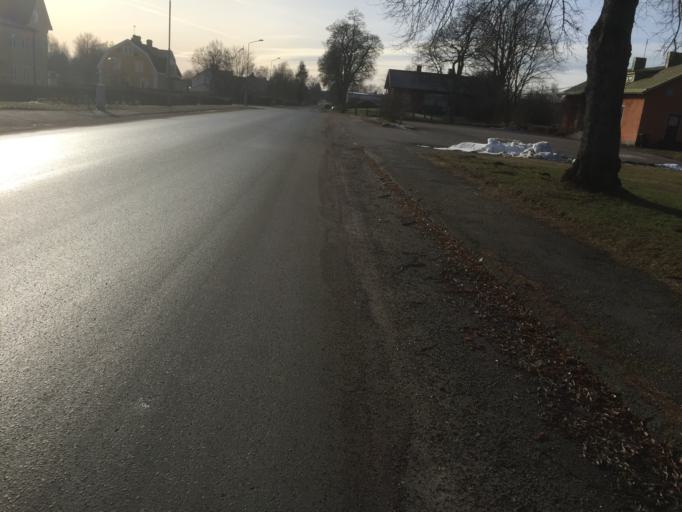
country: SE
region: Joenkoeping
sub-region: Aneby Kommun
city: Aneby
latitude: 57.8366
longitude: 14.8120
